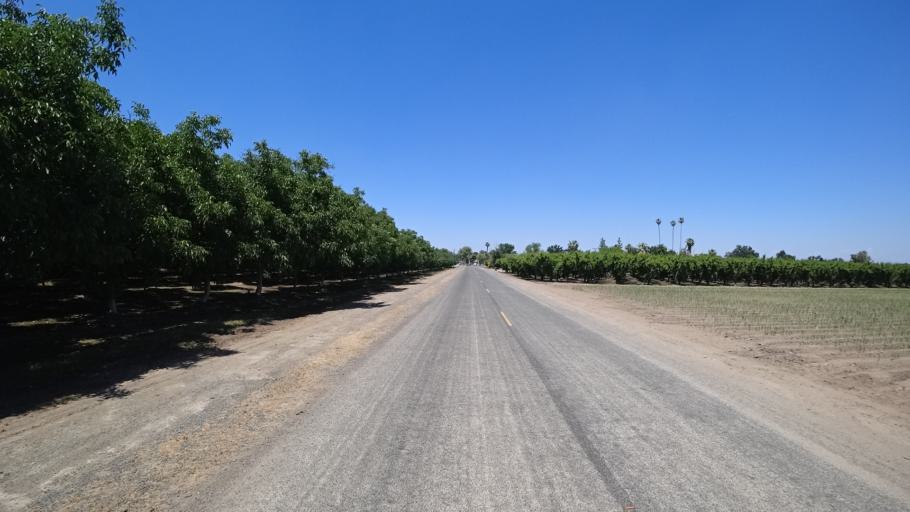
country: US
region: California
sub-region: Fresno County
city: Laton
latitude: 36.4207
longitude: -119.6952
